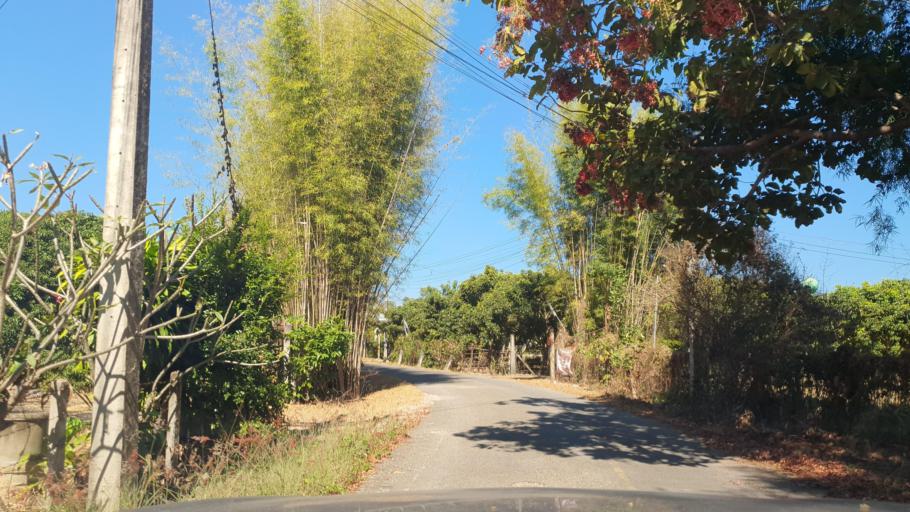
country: TH
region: Chiang Mai
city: San Pa Tong
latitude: 18.6476
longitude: 98.8438
